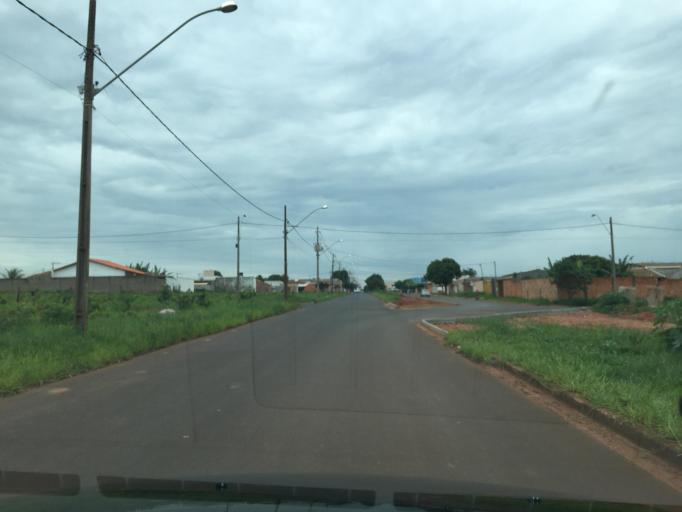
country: BR
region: Minas Gerais
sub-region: Uberlandia
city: Uberlandia
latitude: -18.8678
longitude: -48.2237
